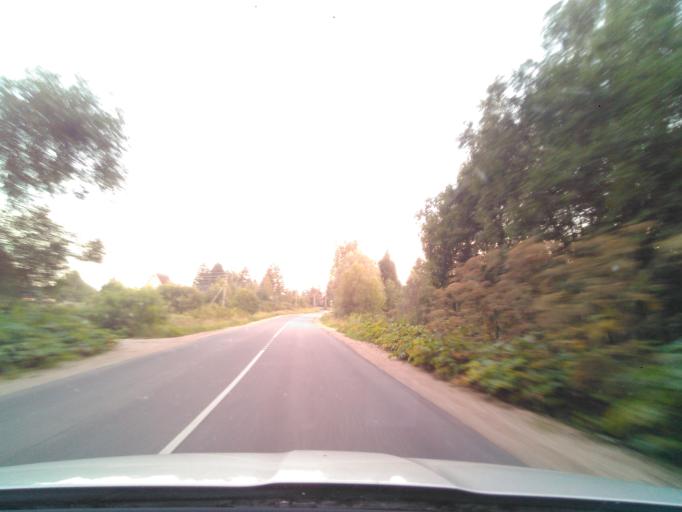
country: RU
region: Moskovskaya
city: Klin
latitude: 56.2466
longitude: 36.8335
